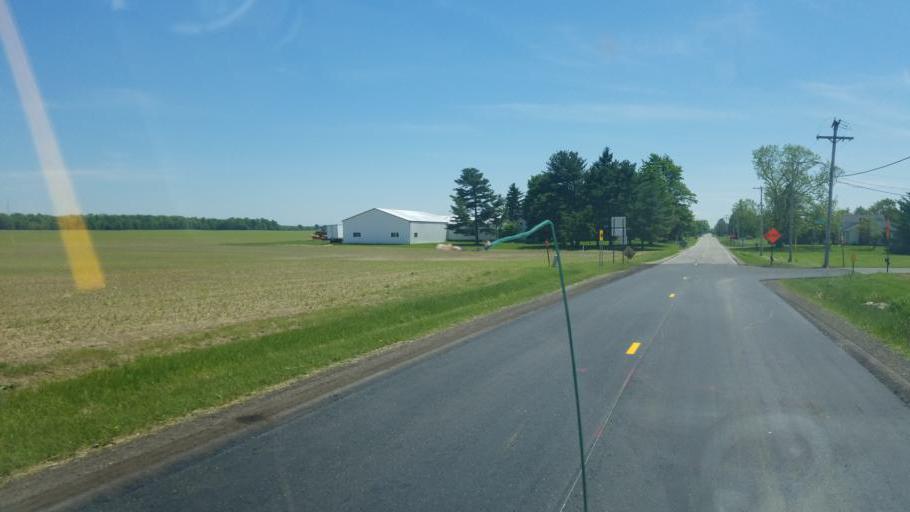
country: US
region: Ohio
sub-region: Huron County
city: Norwalk
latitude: 41.1915
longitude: -82.5900
